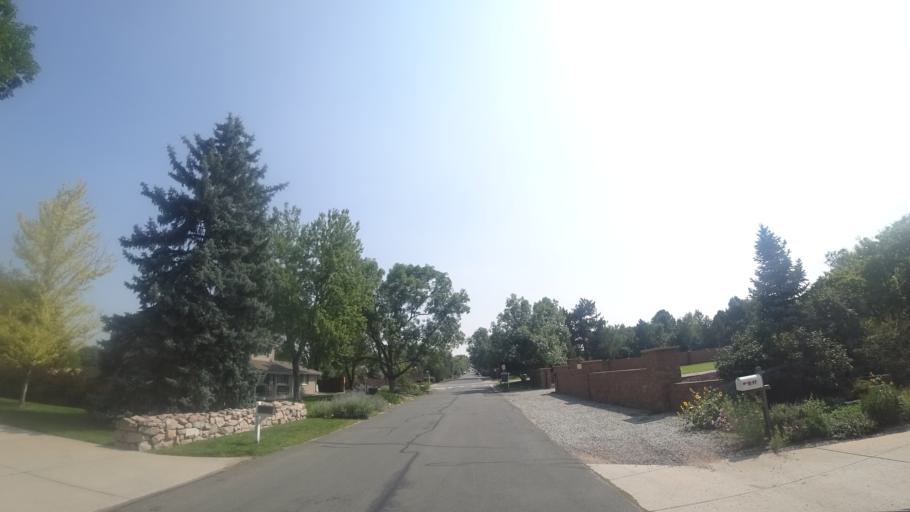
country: US
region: Colorado
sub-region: Arapahoe County
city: Cherry Hills Village
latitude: 39.6249
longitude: -104.9691
